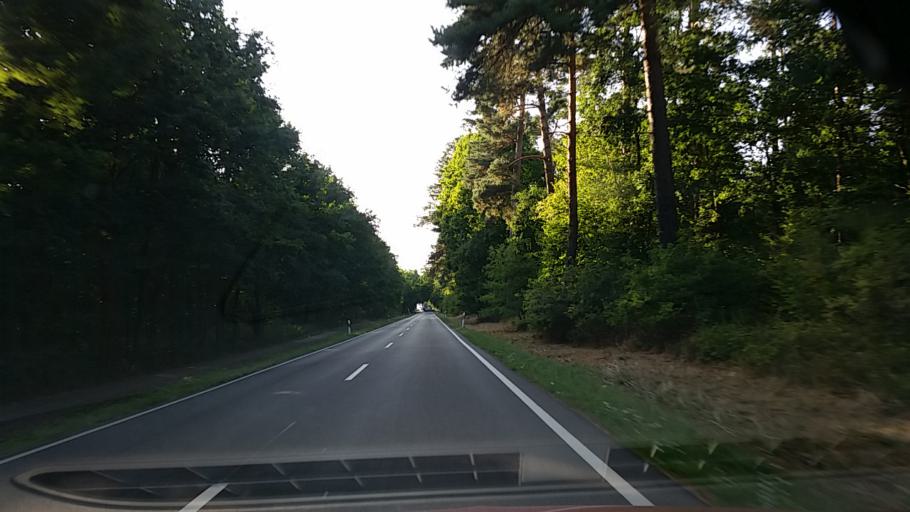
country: DE
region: Lower Saxony
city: Lehre
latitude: 52.3138
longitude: 10.6462
